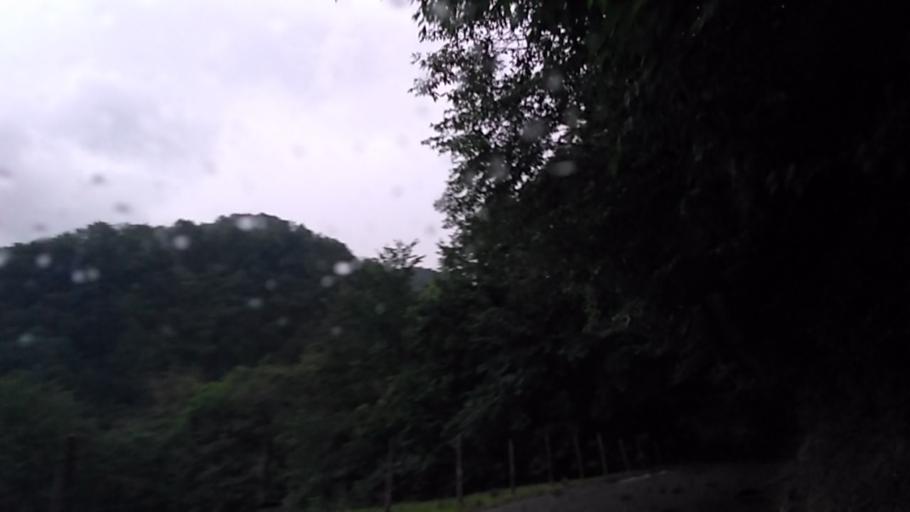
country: IT
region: Lombardy
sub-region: Provincia di Brescia
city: Gardola
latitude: 45.7794
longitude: 10.7150
